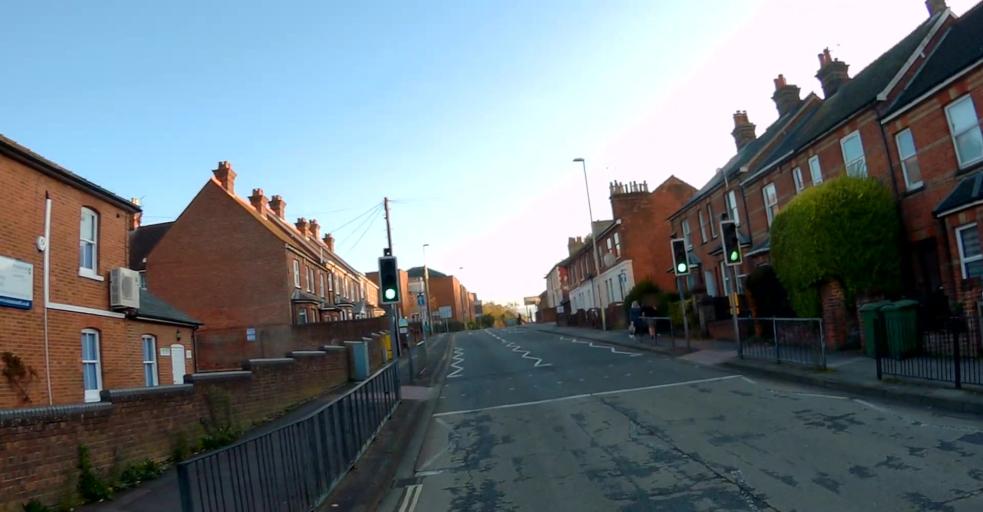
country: GB
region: England
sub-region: Hampshire
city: Basingstoke
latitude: 51.2639
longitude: -1.0843
